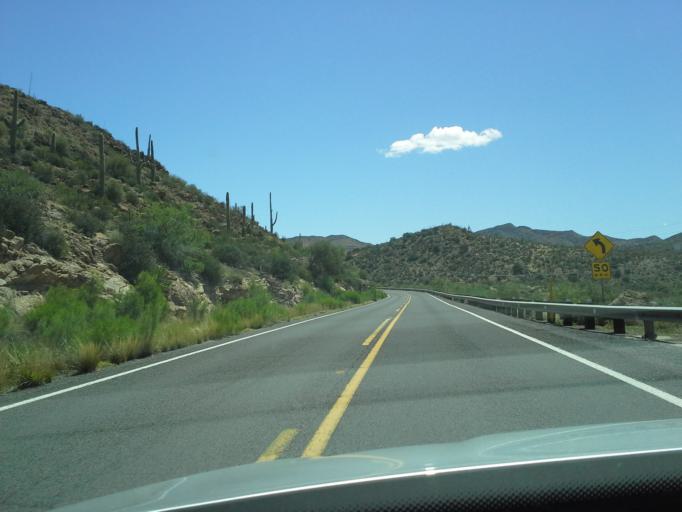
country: US
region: Arizona
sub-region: Pinal County
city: Superior
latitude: 33.2292
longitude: -111.0859
